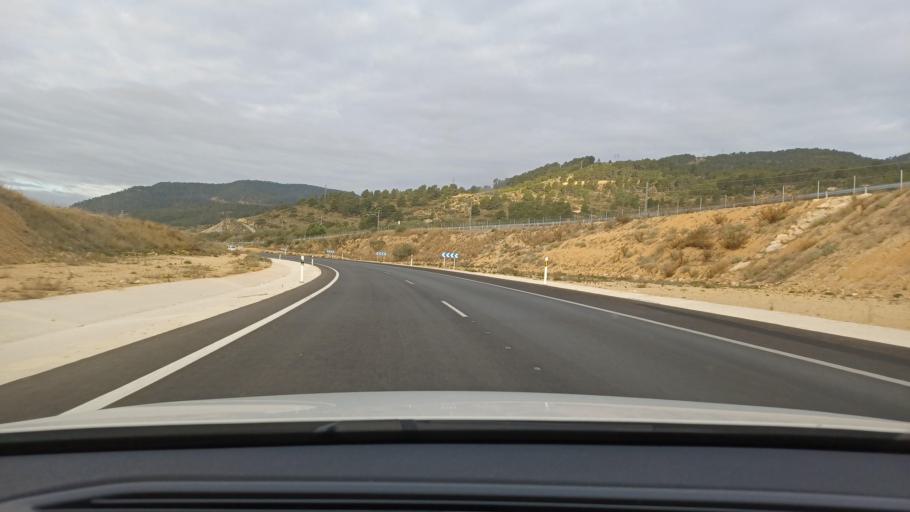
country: ES
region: Valencia
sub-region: Provincia de Valencia
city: La Font de la Figuera
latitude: 38.8306
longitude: -0.8870
